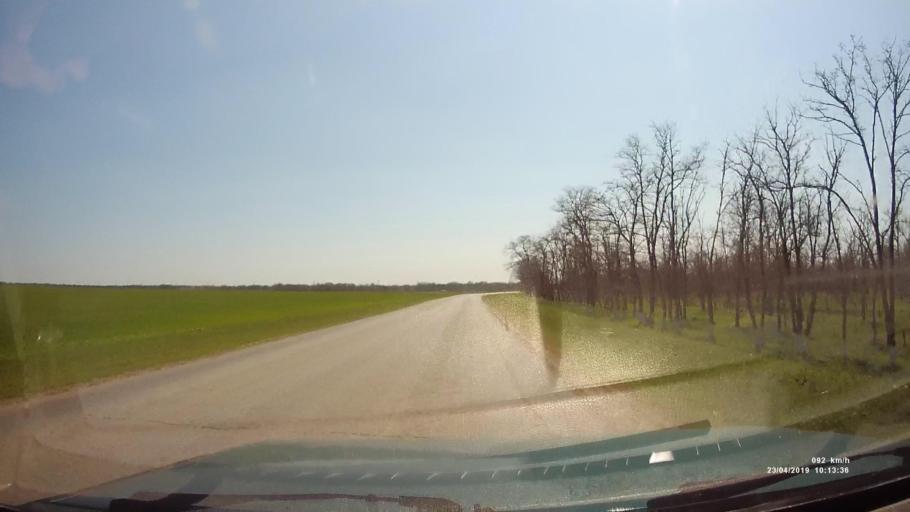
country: RU
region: Rostov
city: Sovetskoye
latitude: 46.6840
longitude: 42.3584
